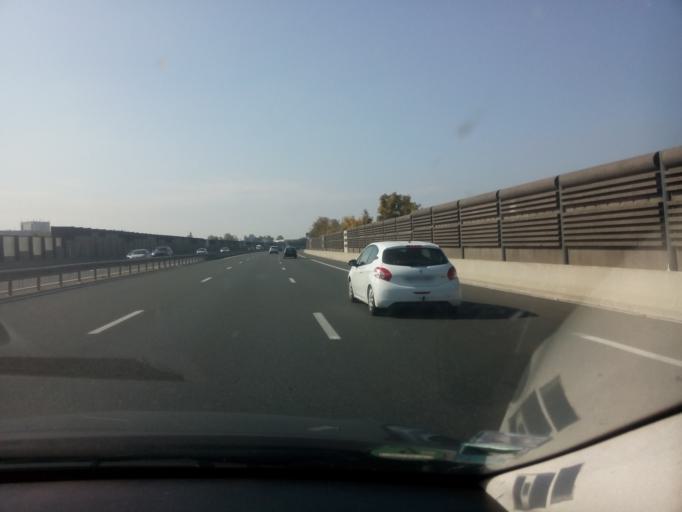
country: FR
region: Pays de la Loire
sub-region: Departement de Maine-et-Loire
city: Ecouflant
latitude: 47.4952
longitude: -0.5240
